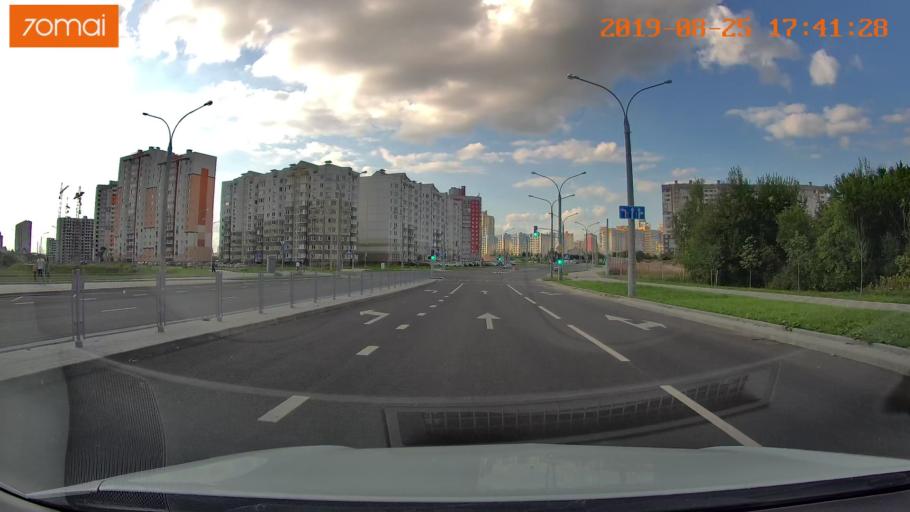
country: BY
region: Minsk
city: Novoye Medvezhino
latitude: 53.8722
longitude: 27.4577
